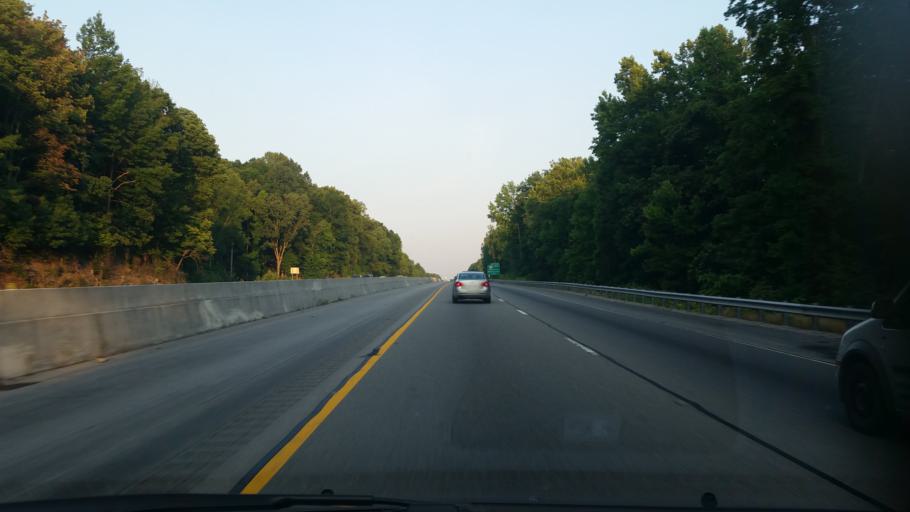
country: US
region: Tennessee
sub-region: Putnam County
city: Lafayette
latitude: 36.0999
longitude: -85.7441
